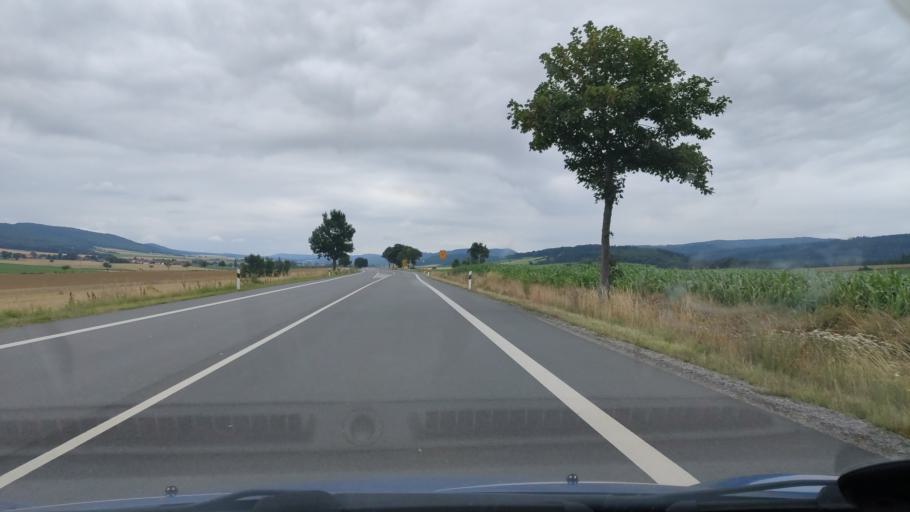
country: DE
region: Lower Saxony
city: Halle
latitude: 51.9813
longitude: 9.5768
